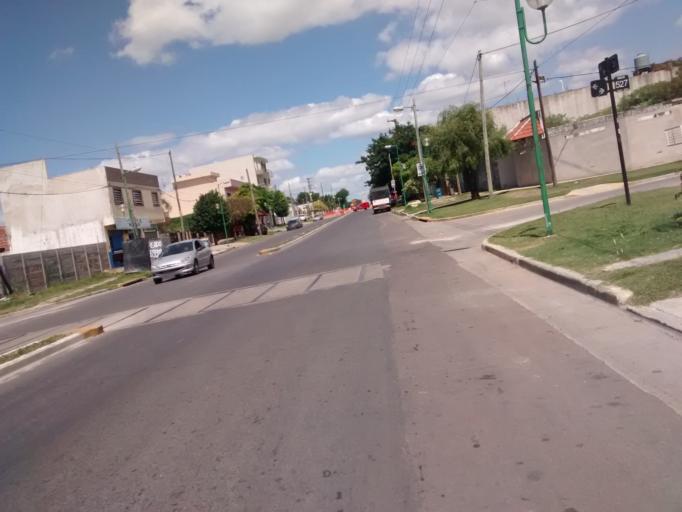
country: AR
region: Buenos Aires
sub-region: Partido de La Plata
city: La Plata
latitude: -34.9187
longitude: -57.9995
